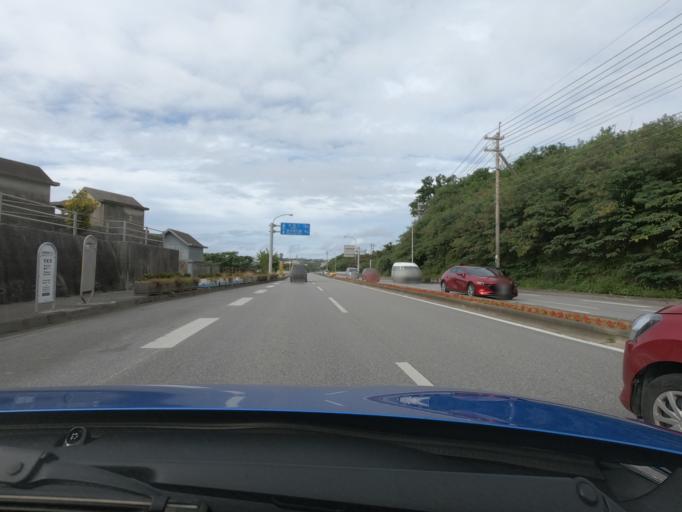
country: JP
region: Okinawa
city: Nago
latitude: 26.6646
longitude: 127.8910
